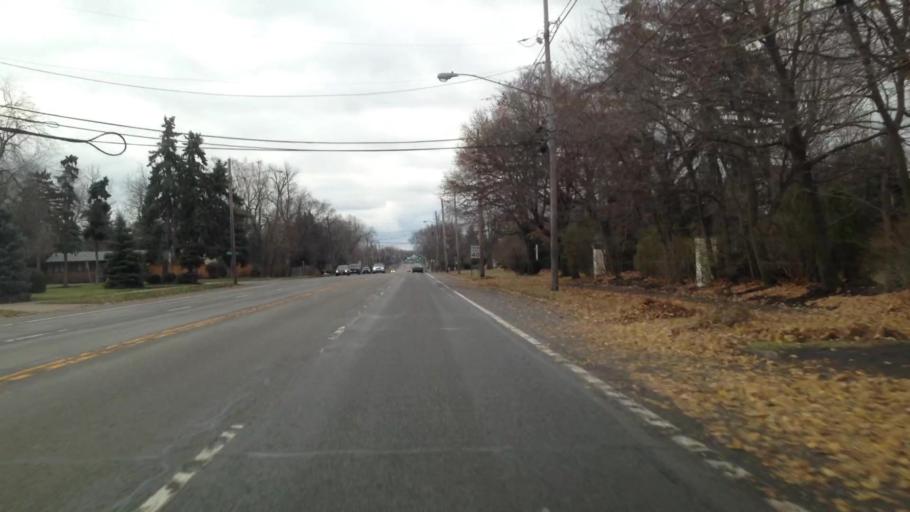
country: US
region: New York
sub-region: Erie County
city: Eggertsville
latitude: 42.9642
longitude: -78.7972
